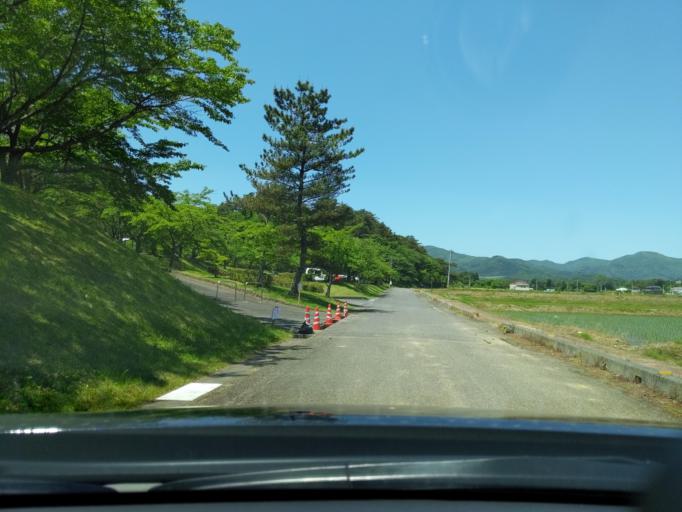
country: JP
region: Fukushima
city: Koriyama
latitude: 37.3893
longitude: 140.2777
